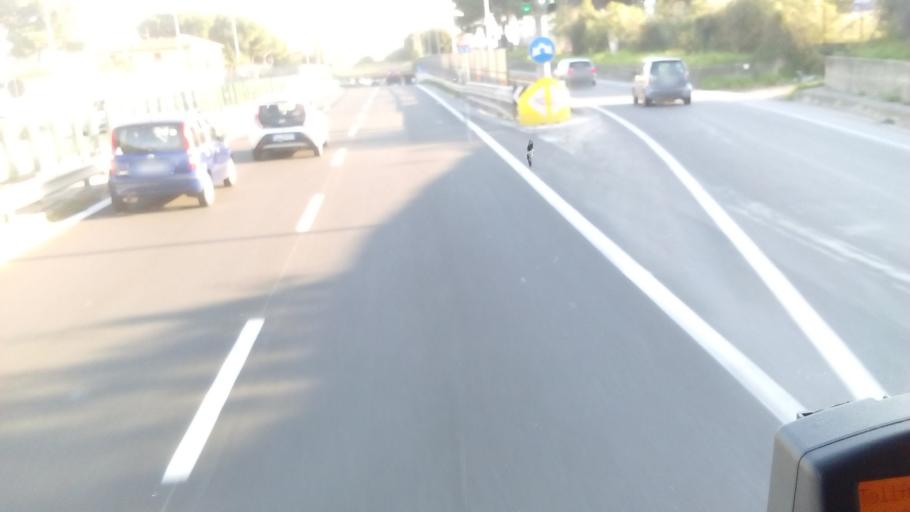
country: IT
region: Latium
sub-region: Citta metropolitana di Roma Capitale
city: Ciampino
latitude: 41.7902
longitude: 12.5945
